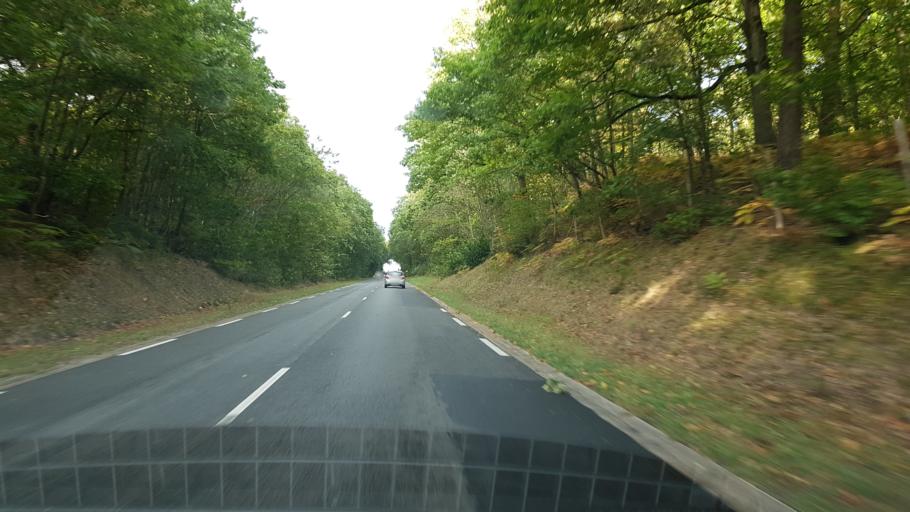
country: FR
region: Ile-de-France
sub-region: Departement de l'Essonne
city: Fontenay-les-Briis
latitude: 48.6277
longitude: 2.1747
